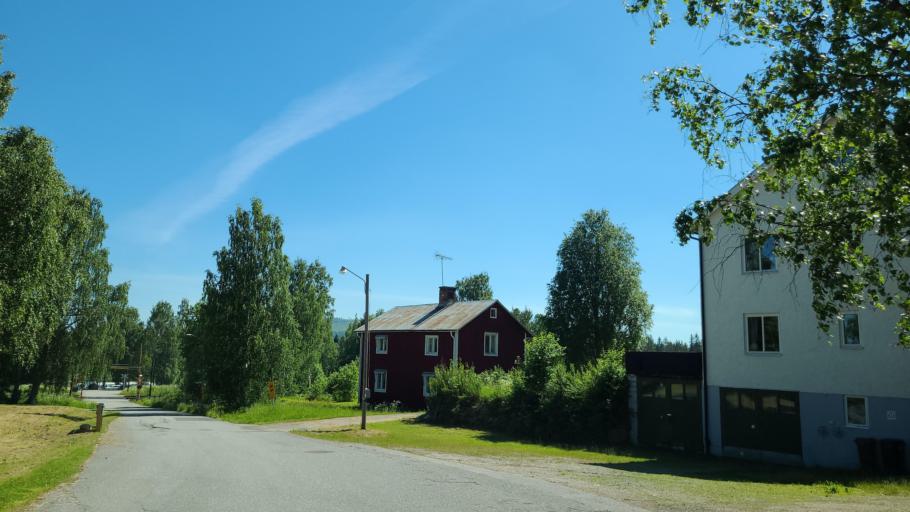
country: SE
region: Vaesterbotten
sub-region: Bjurholms Kommun
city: Bjurholm
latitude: 63.6919
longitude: 18.8630
